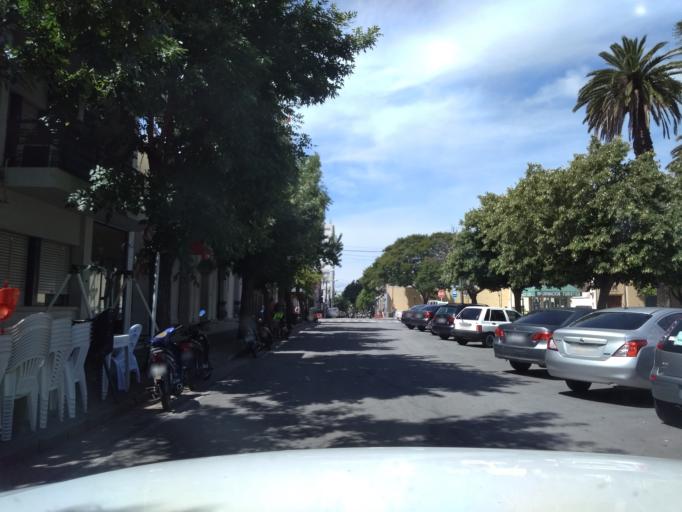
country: UY
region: Florida
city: Florida
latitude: -34.1007
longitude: -56.2152
